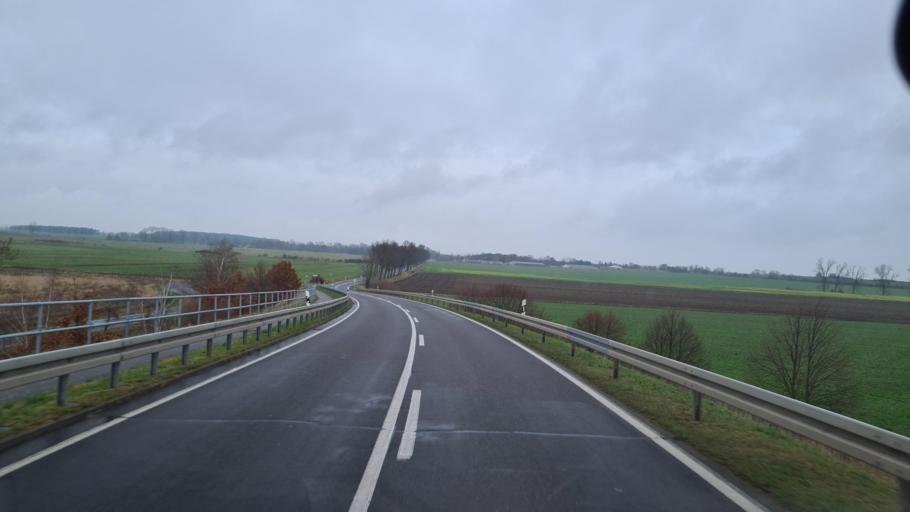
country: DE
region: Brandenburg
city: Retzow
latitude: 52.5926
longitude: 12.6408
